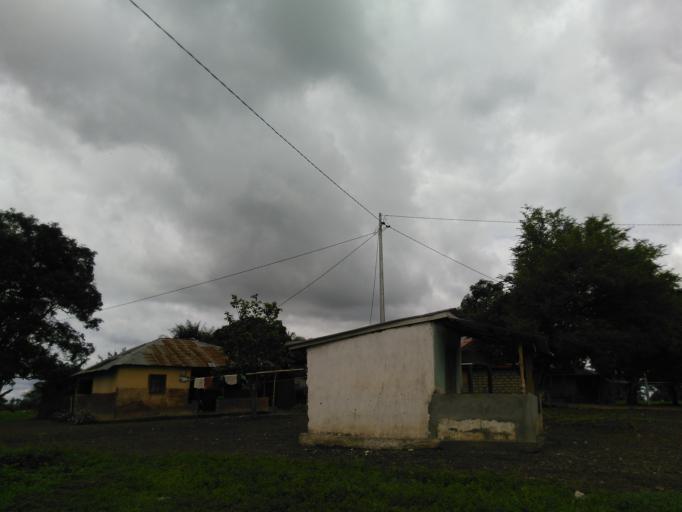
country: SL
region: Northern Province
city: Rokupr
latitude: 8.6456
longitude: -12.4501
